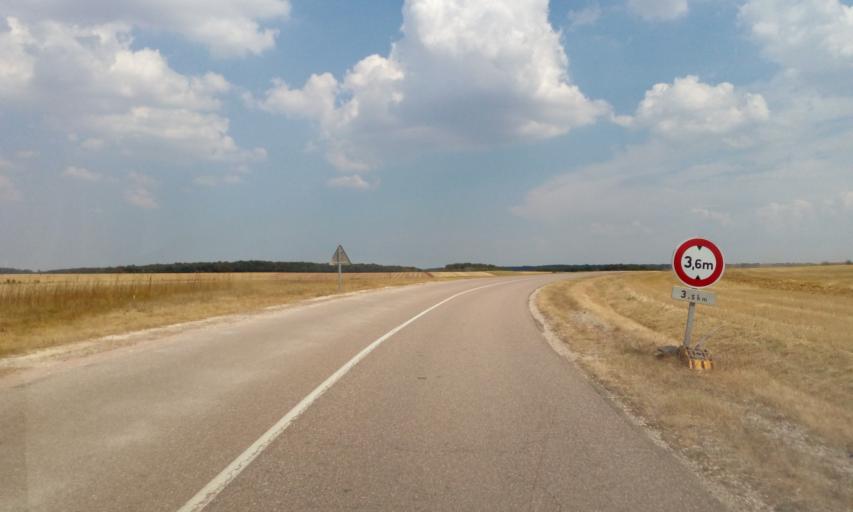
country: FR
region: Lorraine
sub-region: Departement de la Meuse
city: Vigneulles-les-Hattonchatel
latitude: 48.9681
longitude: 5.8625
